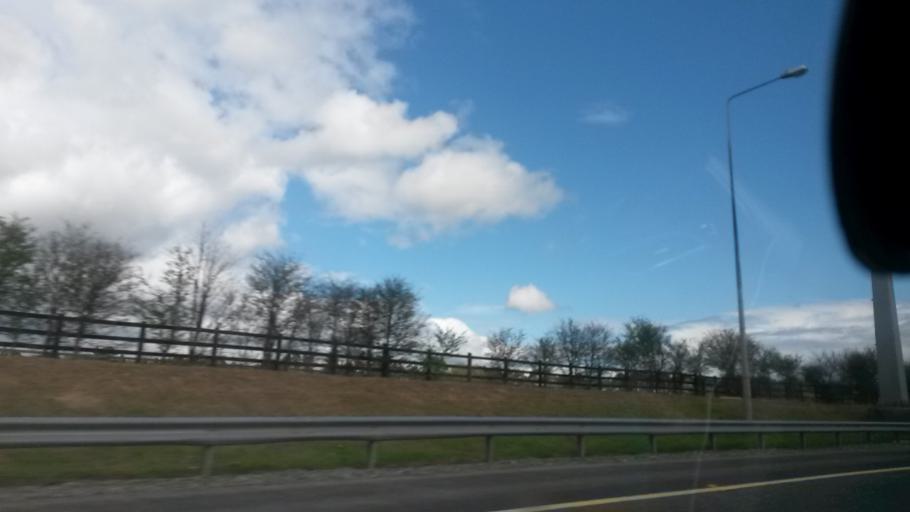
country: IE
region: Leinster
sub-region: Kildare
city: Athgarvan
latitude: 53.1616
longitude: -6.8321
